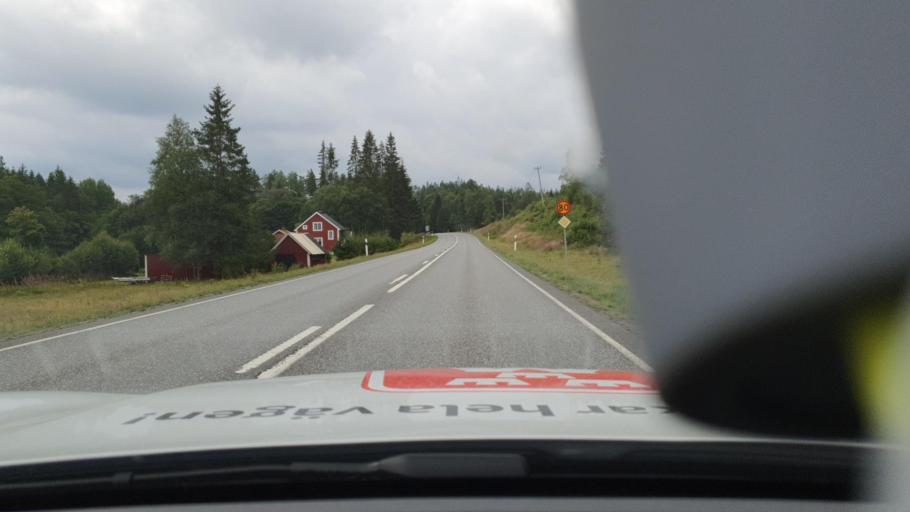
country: SE
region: Joenkoeping
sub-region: Gislaveds Kommun
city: Smalandsstenar
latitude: 57.1939
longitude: 13.4387
